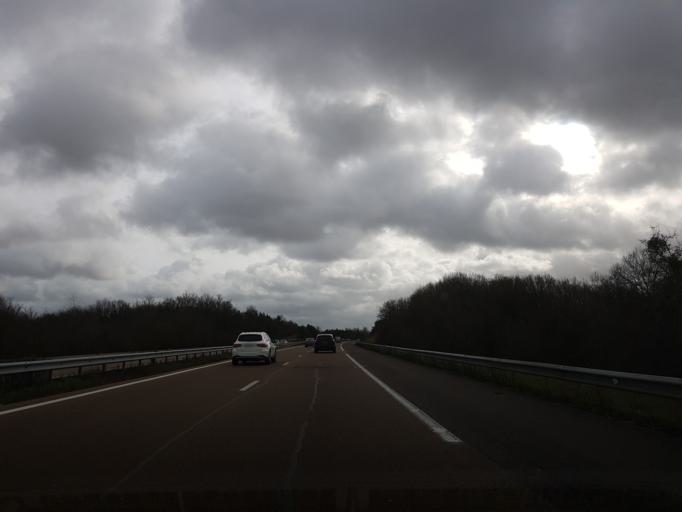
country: FR
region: Champagne-Ardenne
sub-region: Departement de la Haute-Marne
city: Rolampont
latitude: 47.9241
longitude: 5.2177
